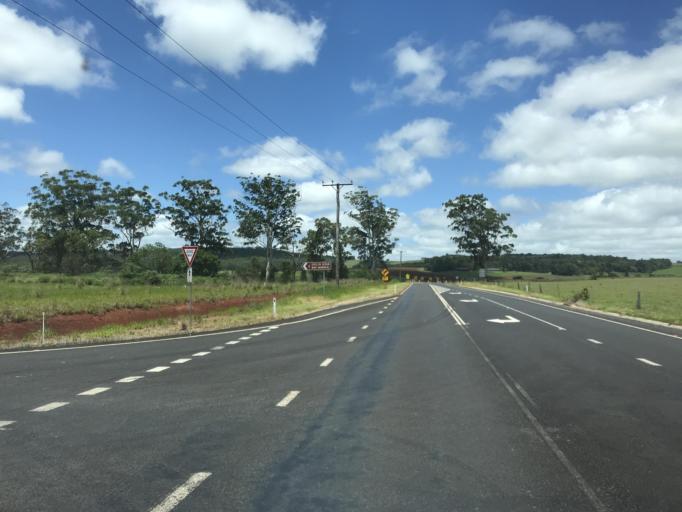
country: AU
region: Queensland
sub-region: Tablelands
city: Ravenshoe
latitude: -17.5092
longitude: 145.4554
